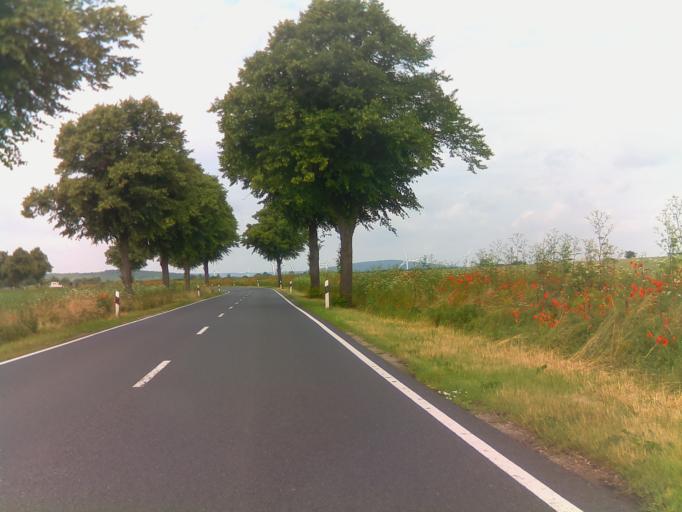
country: DE
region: Lower Saxony
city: Pattensen
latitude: 52.2099
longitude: 9.7355
